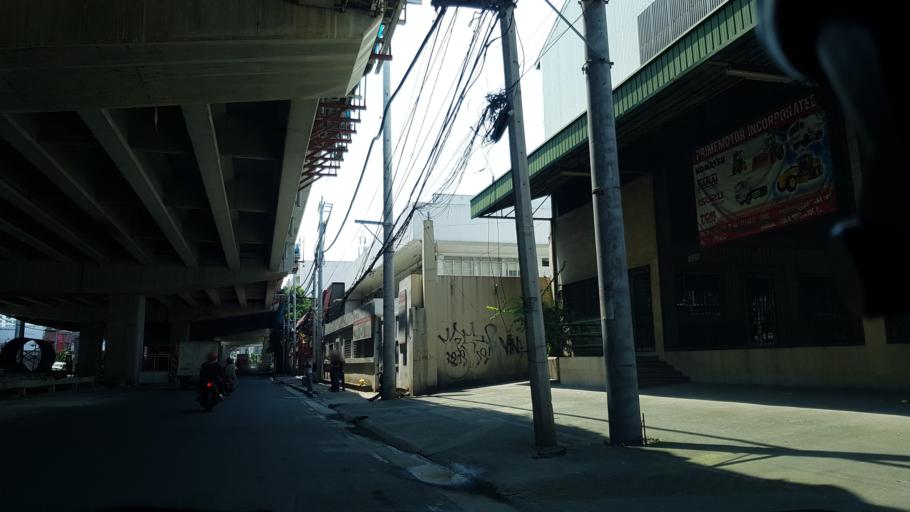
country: PH
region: Calabarzon
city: Del Monte
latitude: 14.6359
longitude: 121.0087
